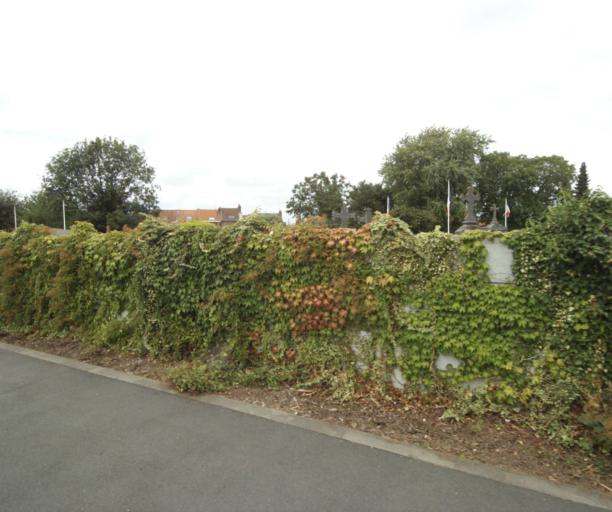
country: FR
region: Nord-Pas-de-Calais
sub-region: Departement du Nord
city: Villeneuve-d'Ascq
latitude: 50.6189
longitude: 3.1663
